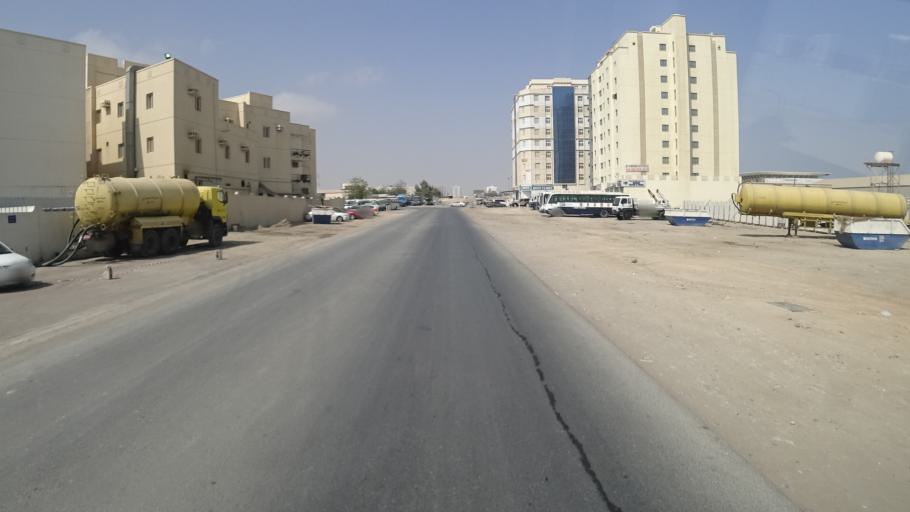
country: OM
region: Muhafazat Masqat
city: Bawshar
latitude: 23.5797
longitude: 58.3564
